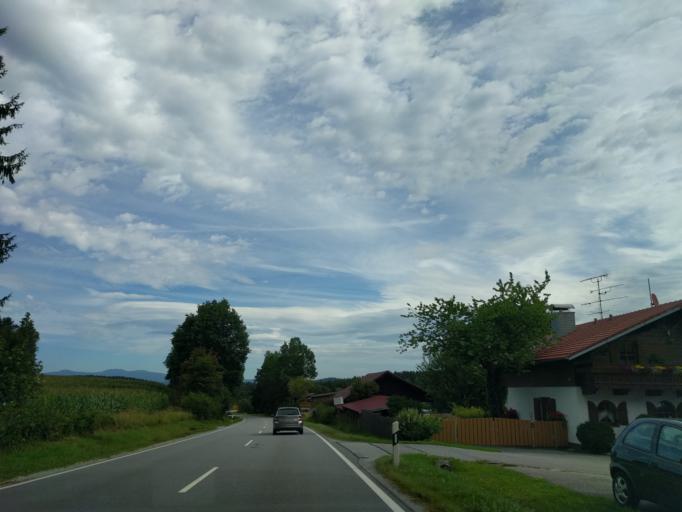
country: DE
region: Bavaria
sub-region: Lower Bavaria
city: Bischofsmais
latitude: 48.8981
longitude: 13.0935
